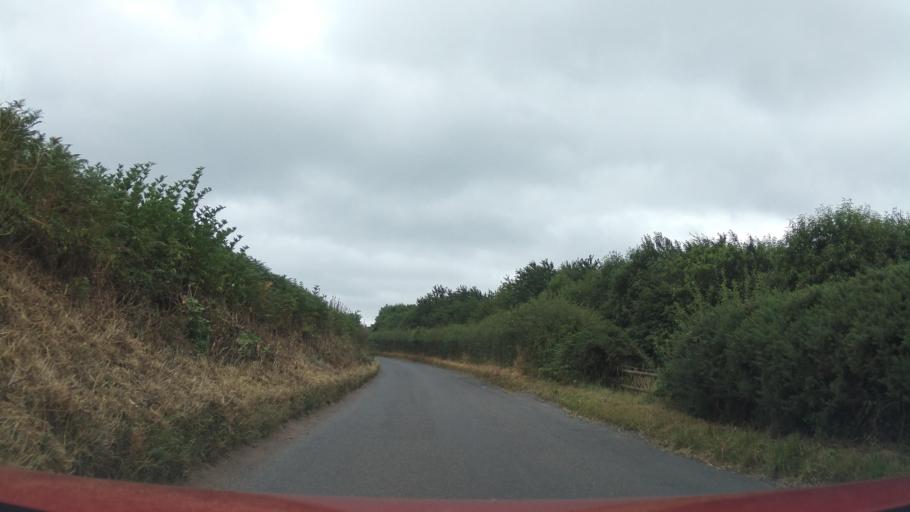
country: GB
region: England
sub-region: Derbyshire
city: Swadlincote
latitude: 52.7777
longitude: -1.5097
